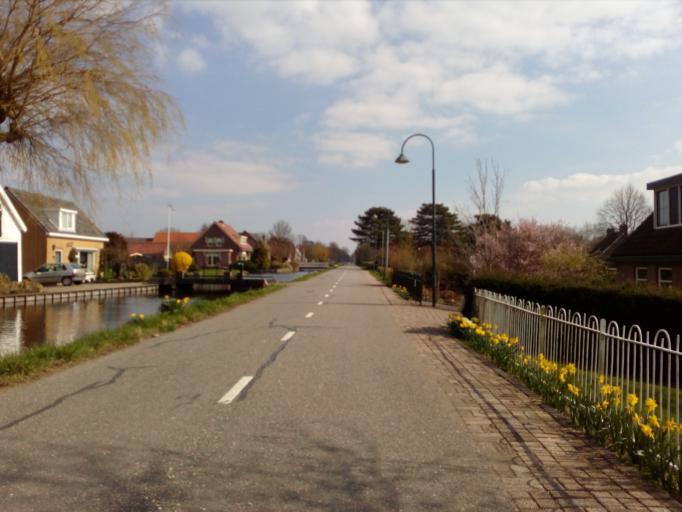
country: NL
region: South Holland
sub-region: Gemeente Zoetermeer
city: Zoetermeer
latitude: 52.0636
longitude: 4.4589
